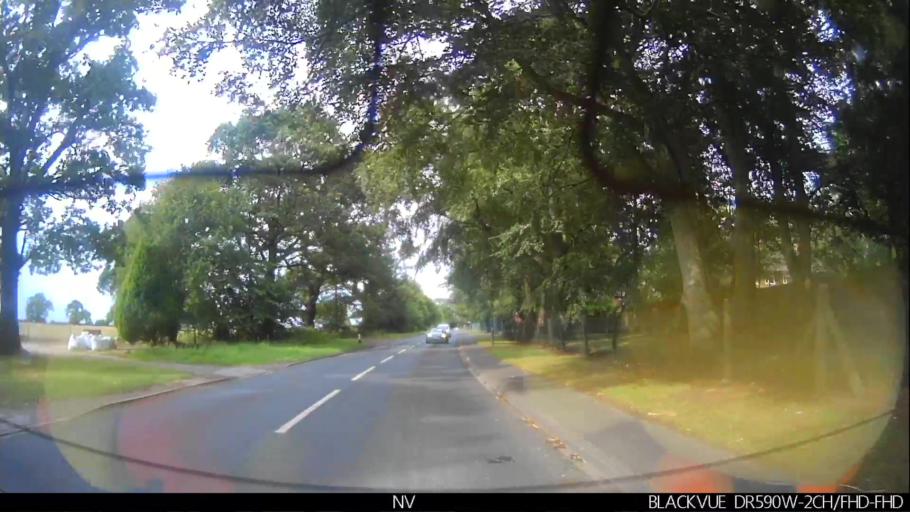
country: GB
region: England
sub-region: North Yorkshire
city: Strensall
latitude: 54.0232
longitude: -1.0443
